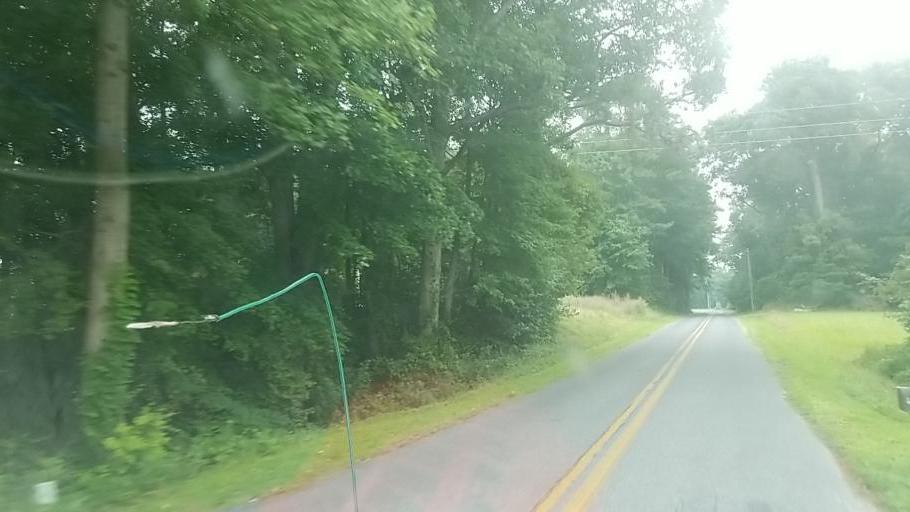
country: US
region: Maryland
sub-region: Worcester County
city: Ocean Pines
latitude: 38.4232
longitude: -75.1911
